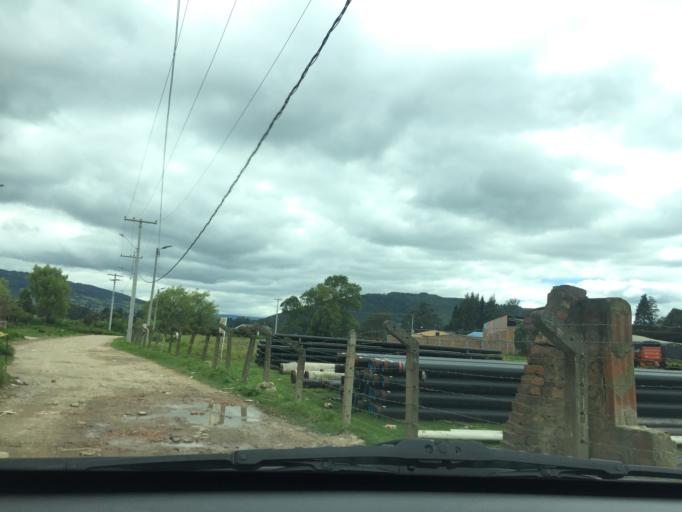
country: CO
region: Cundinamarca
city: Zipaquira
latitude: 5.0224
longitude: -73.9832
